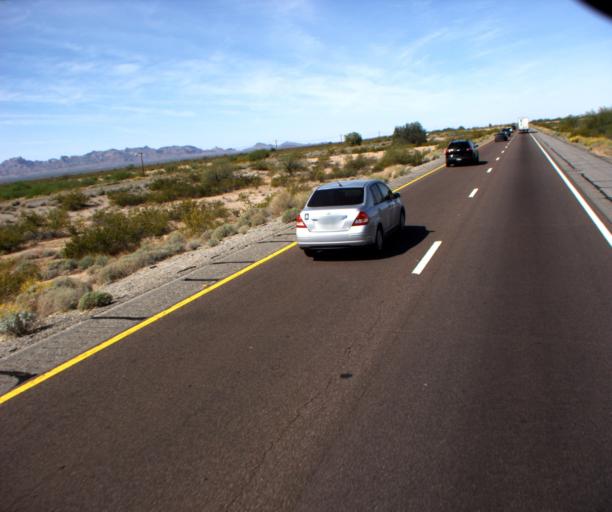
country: US
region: Arizona
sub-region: La Paz County
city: Salome
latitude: 33.5560
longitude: -113.2656
